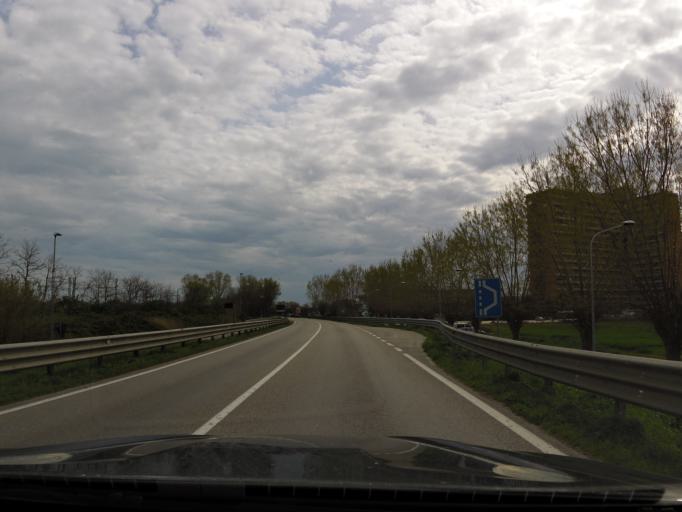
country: IT
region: The Marches
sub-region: Provincia di Macerata
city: Porto Recanati
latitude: 43.4195
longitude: 13.6656
